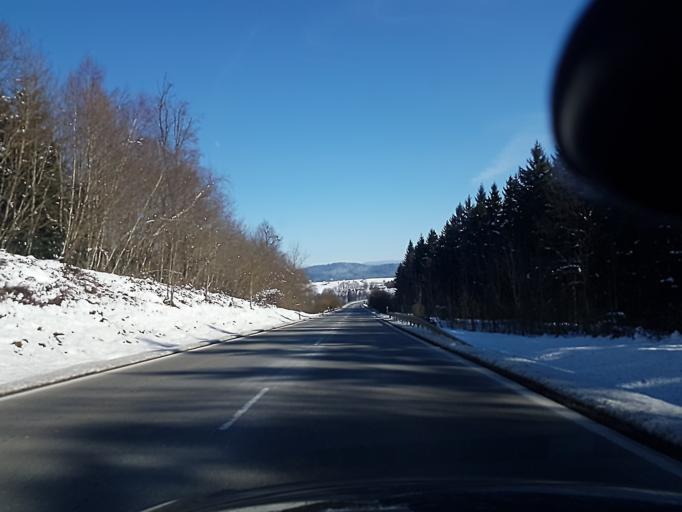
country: DE
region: Baden-Wuerttemberg
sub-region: Freiburg Region
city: Rottweil
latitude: 48.1831
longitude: 8.6216
